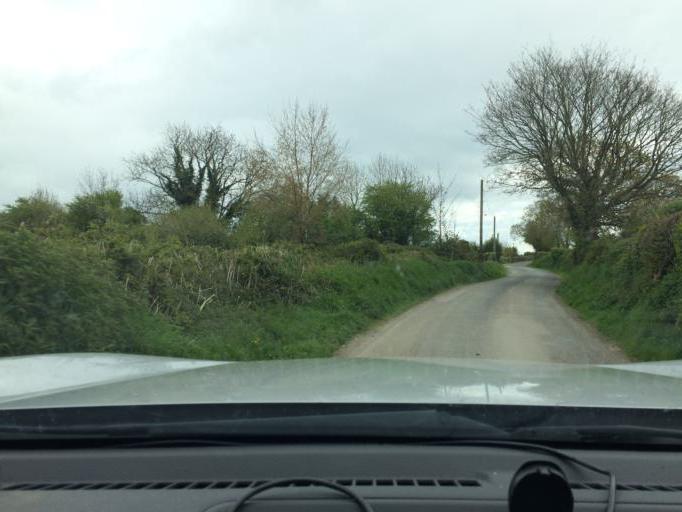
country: IE
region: Munster
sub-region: Waterford
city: Dungarvan
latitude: 52.0551
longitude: -7.6223
